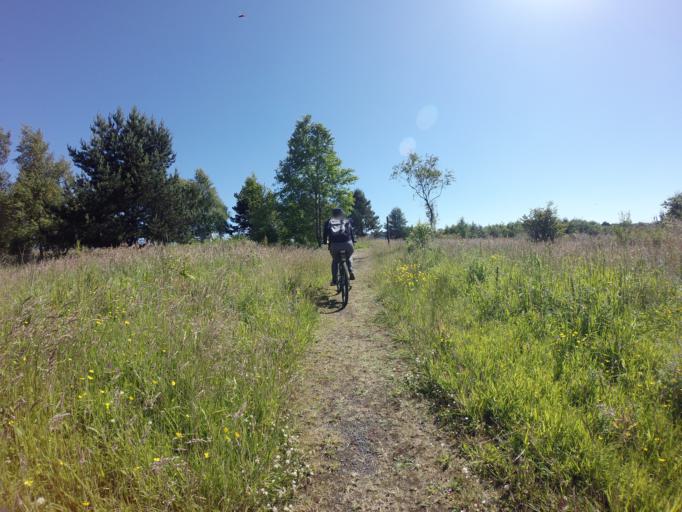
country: GB
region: Scotland
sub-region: West Lothian
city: West Calder
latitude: 55.8940
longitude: -3.5754
